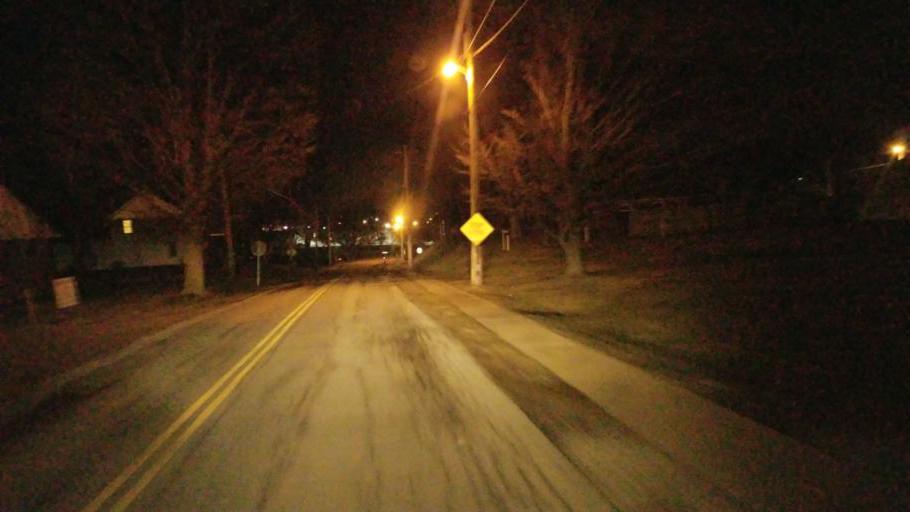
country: US
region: Ohio
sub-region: Huron County
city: Monroeville
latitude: 41.2397
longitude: -82.6938
